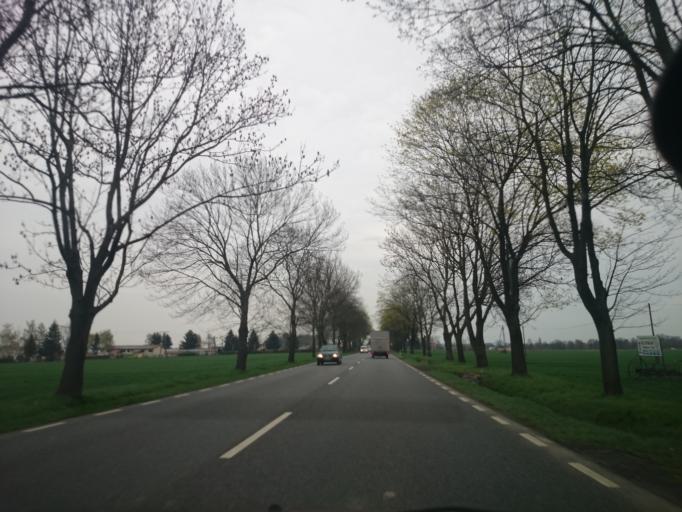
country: PL
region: Opole Voivodeship
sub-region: Powiat nyski
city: Otmuchow
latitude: 50.4476
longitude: 17.1002
